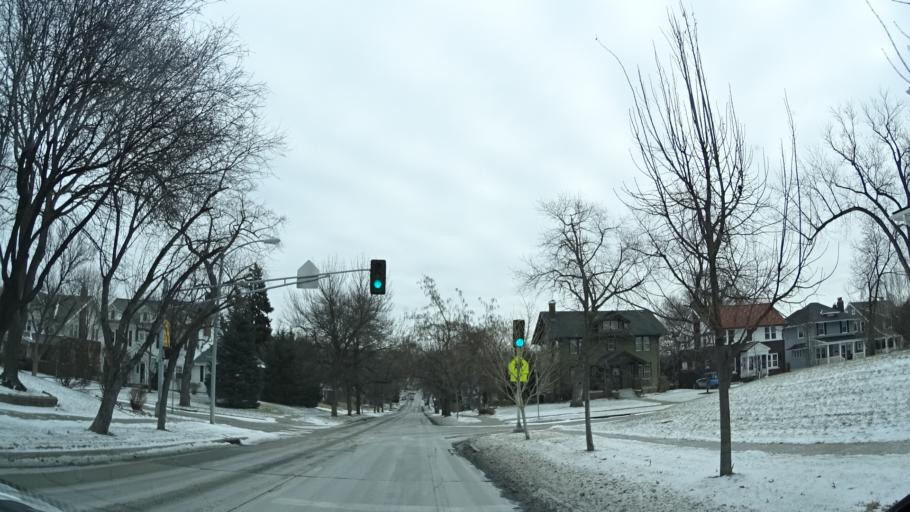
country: US
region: Nebraska
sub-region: Douglas County
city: Omaha
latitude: 41.2579
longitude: -95.9933
